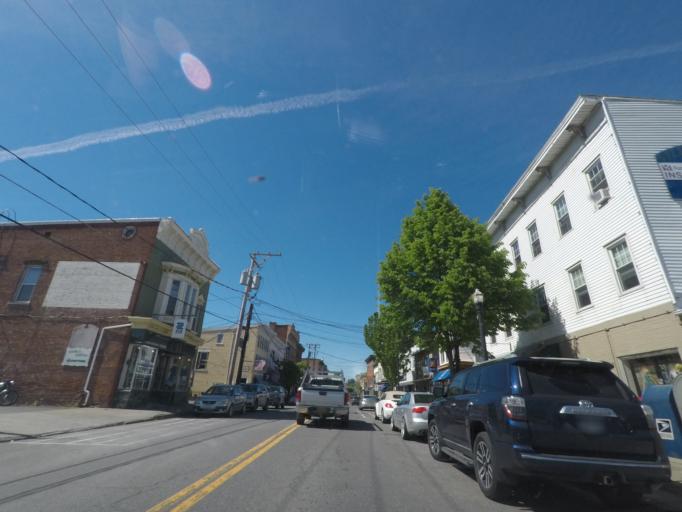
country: US
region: New York
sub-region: Ulster County
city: Saugerties
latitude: 42.0762
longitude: -73.9516
